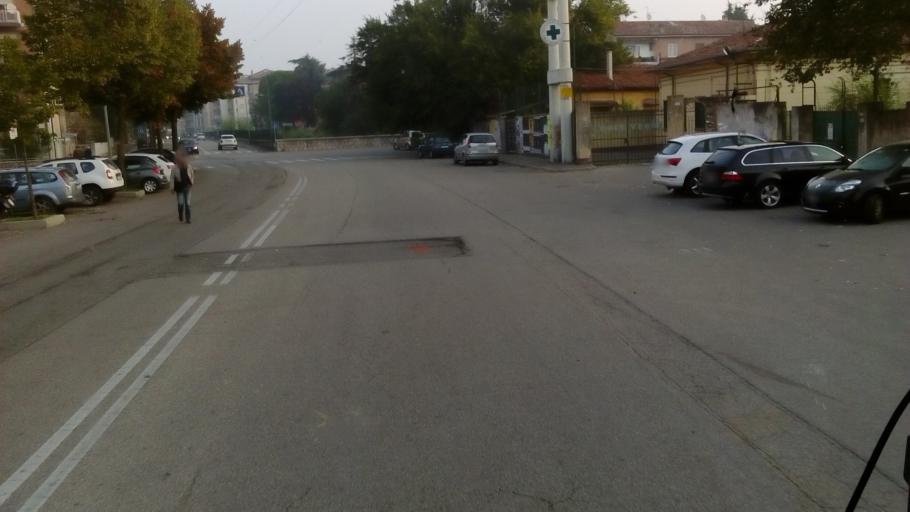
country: IT
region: Veneto
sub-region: Provincia di Verona
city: Poiano
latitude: 45.4367
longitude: 11.0337
